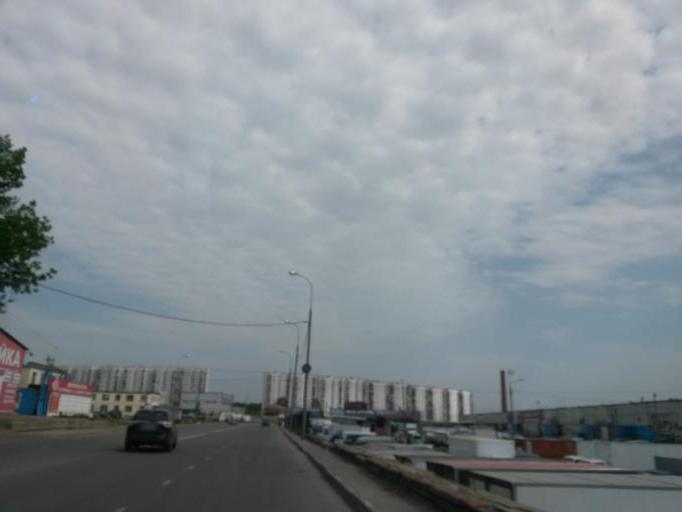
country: RU
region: Moscow
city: Annino
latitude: 55.5809
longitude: 37.5891
